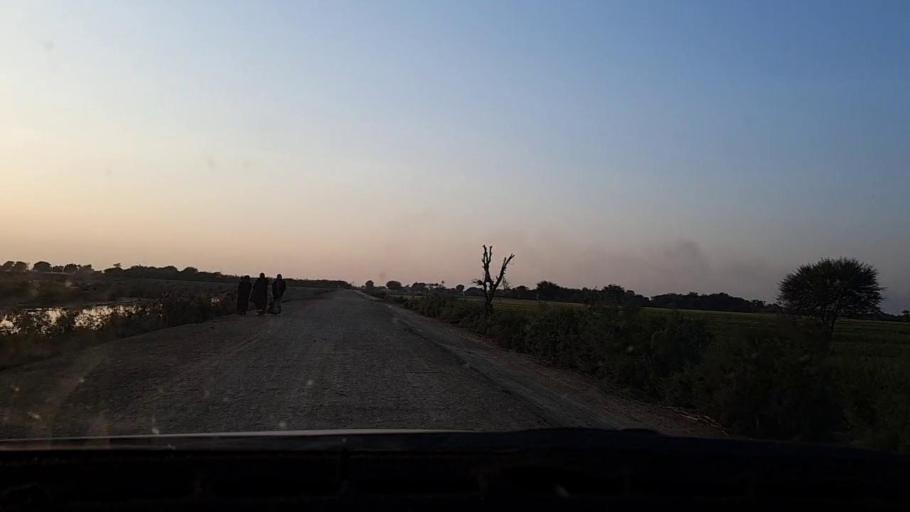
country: PK
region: Sindh
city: Tando Mittha Khan
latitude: 25.8480
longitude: 69.2336
